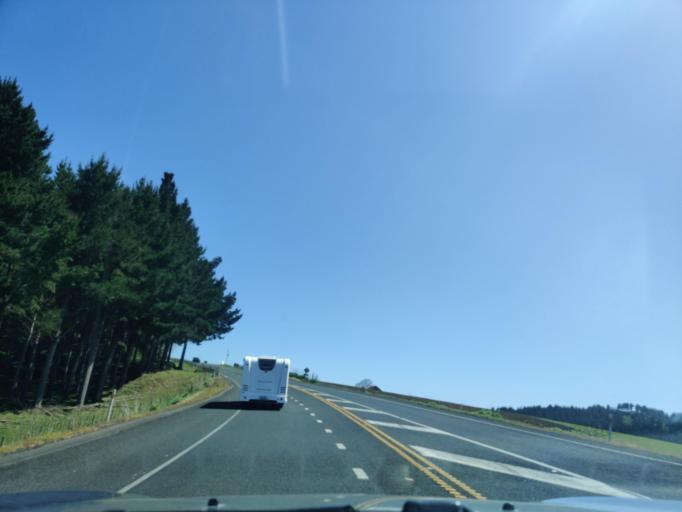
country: NZ
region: Taranaki
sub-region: South Taranaki District
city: Patea
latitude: -39.8047
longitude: 174.7348
